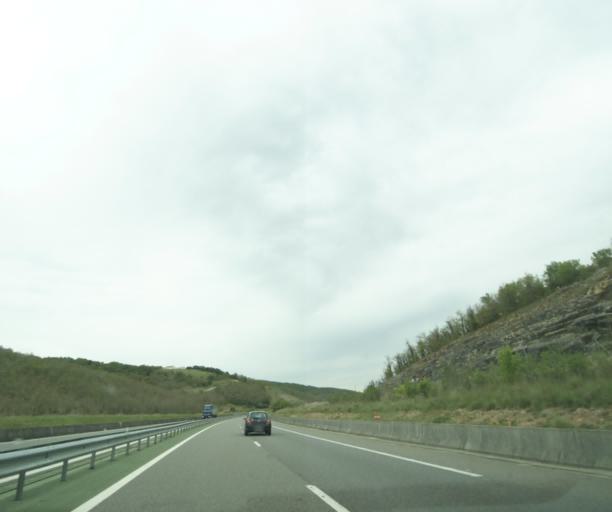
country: FR
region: Midi-Pyrenees
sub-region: Departement du Lot
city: Cahors
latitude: 44.4307
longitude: 1.5047
